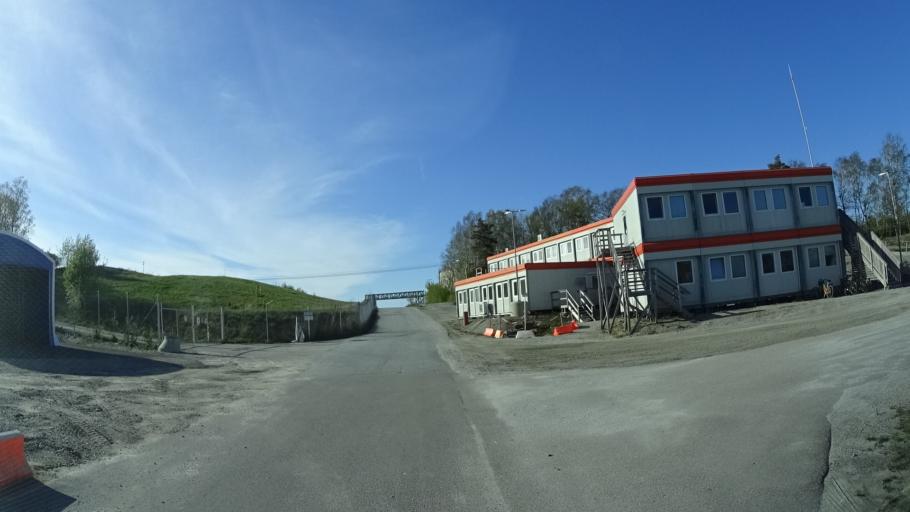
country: SE
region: Vaestra Goetaland
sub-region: Stenungsunds Kommun
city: Stenungsund
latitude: 58.0833
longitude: 11.8159
